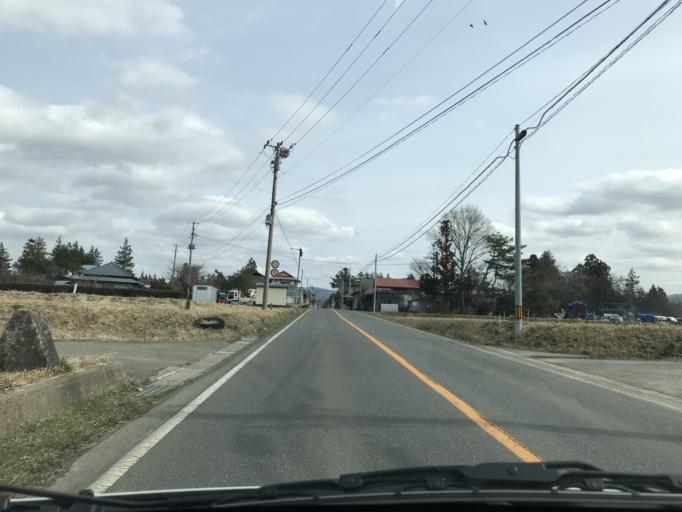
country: JP
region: Iwate
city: Mizusawa
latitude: 39.2173
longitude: 141.2172
